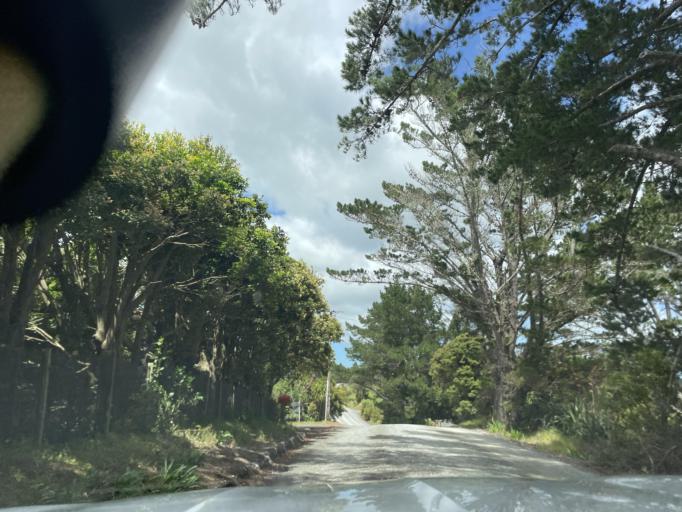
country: NZ
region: Auckland
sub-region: Auckland
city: Wellsford
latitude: -36.1707
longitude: 174.5796
